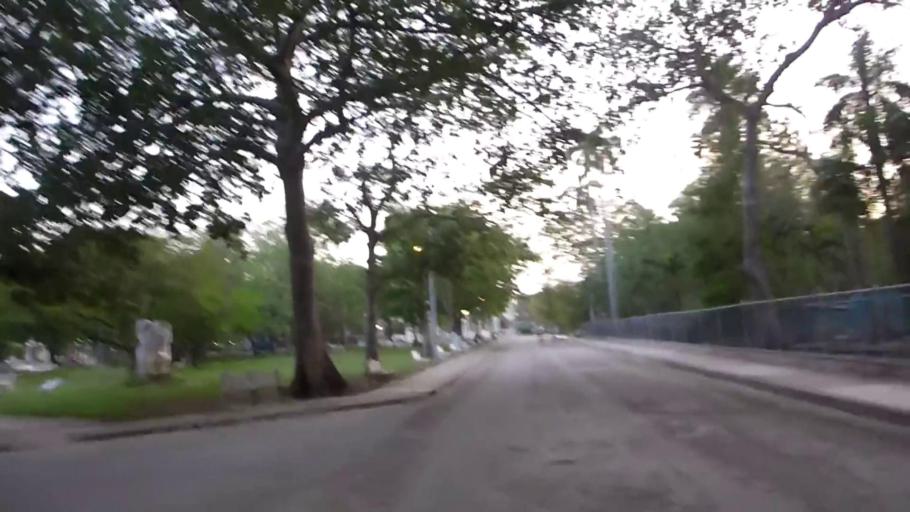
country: CU
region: Camaguey
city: Camaguey
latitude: 21.3772
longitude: -77.9112
